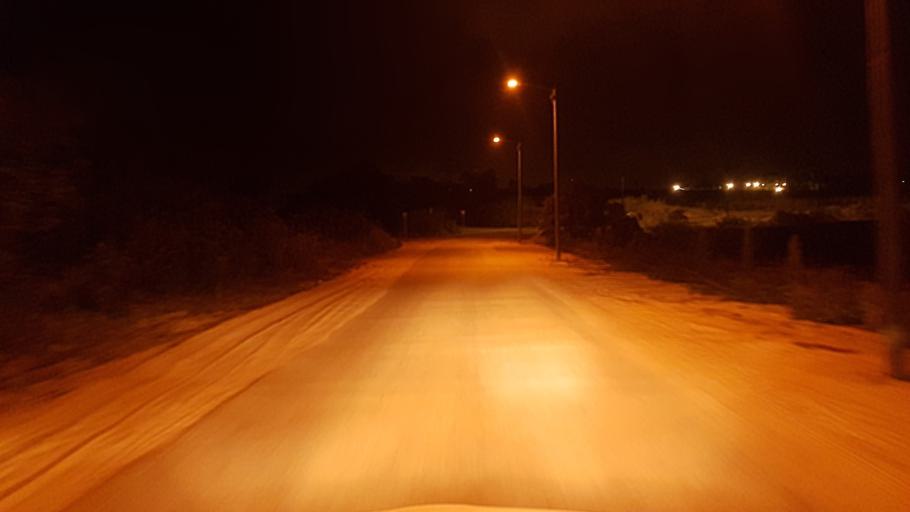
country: IL
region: Central District
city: Hod HaSharon
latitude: 32.1605
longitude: 34.8722
